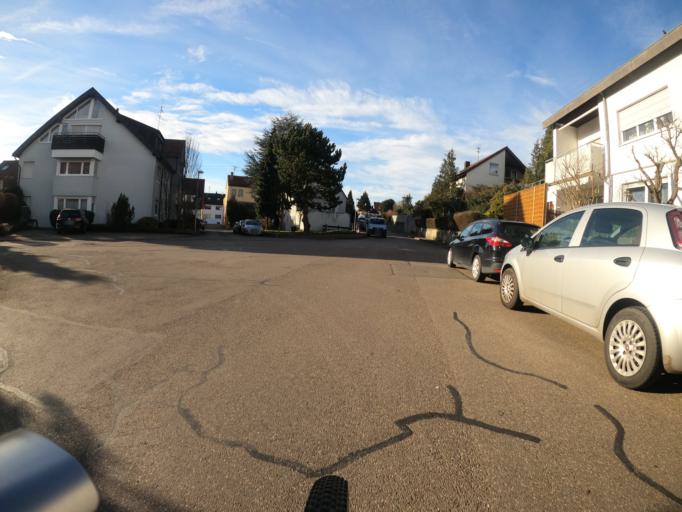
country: DE
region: Baden-Wuerttemberg
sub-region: Regierungsbezirk Stuttgart
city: Wendlingen am Neckar
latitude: 48.6718
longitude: 9.3928
